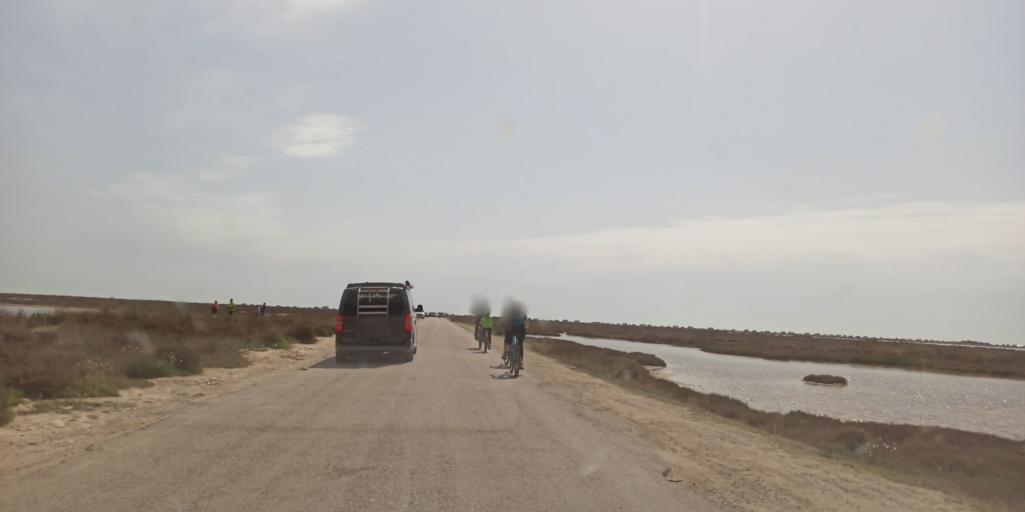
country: ES
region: Catalonia
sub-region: Provincia de Tarragona
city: Deltebre
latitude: 40.6402
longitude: 0.7405
